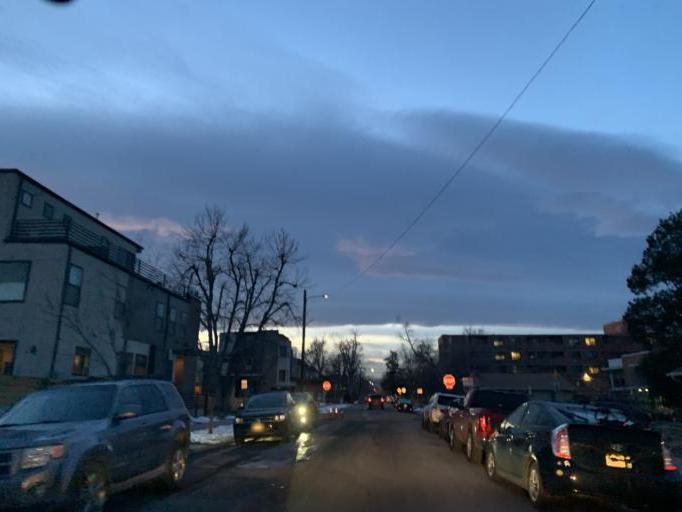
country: US
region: Colorado
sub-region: Jefferson County
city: Edgewater
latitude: 39.7748
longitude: -105.0446
